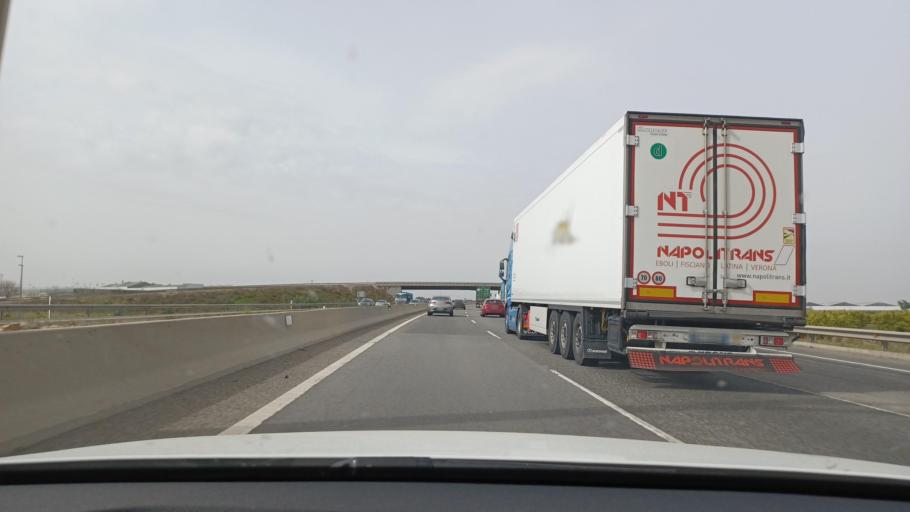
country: ES
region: Valencia
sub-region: Provincia de Valencia
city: Alginet
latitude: 39.2734
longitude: -0.4601
